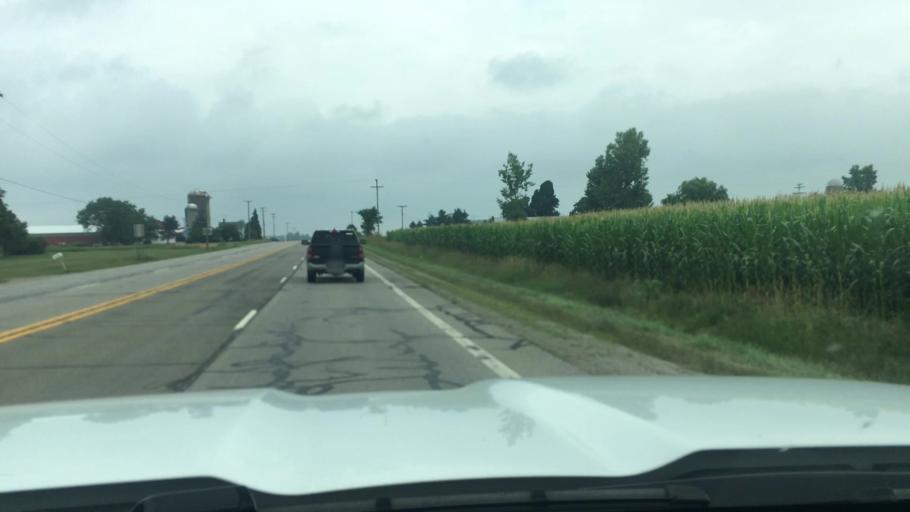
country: US
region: Michigan
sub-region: Sanilac County
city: Brown City
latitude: 43.2234
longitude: -83.0777
